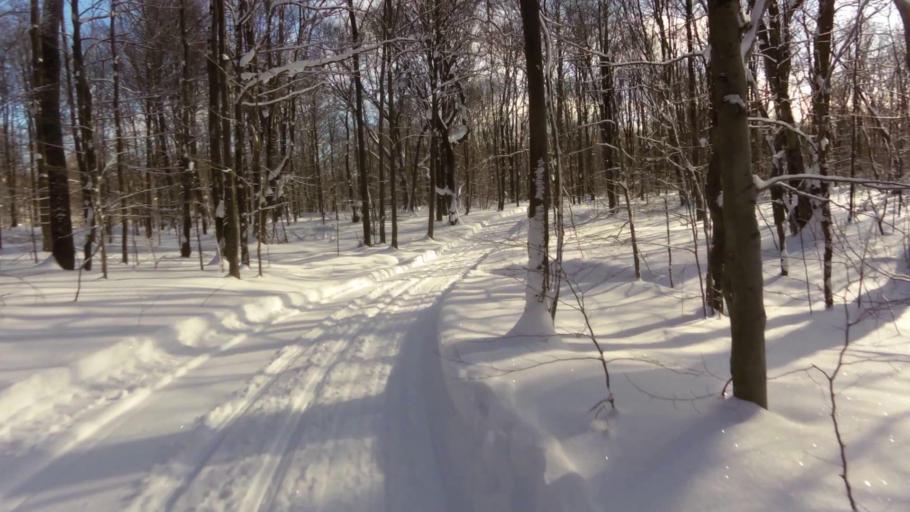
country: US
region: New York
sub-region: Chautauqua County
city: Falconer
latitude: 42.2732
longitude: -79.1331
